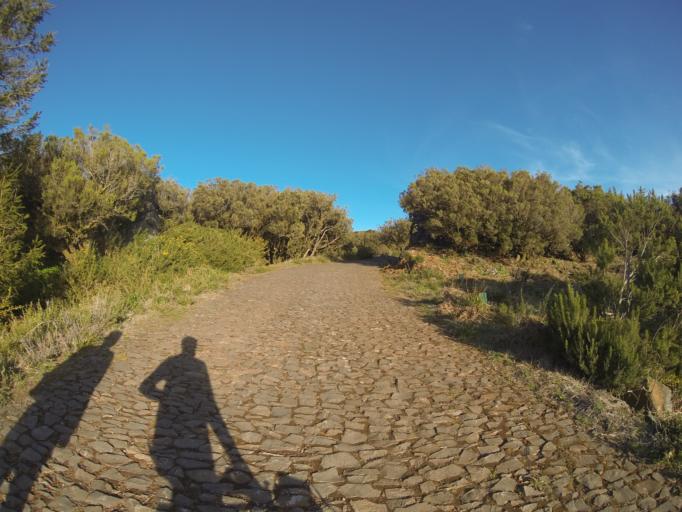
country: PT
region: Madeira
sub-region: Sao Vicente
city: Sao Vicente
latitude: 32.7573
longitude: -17.0586
